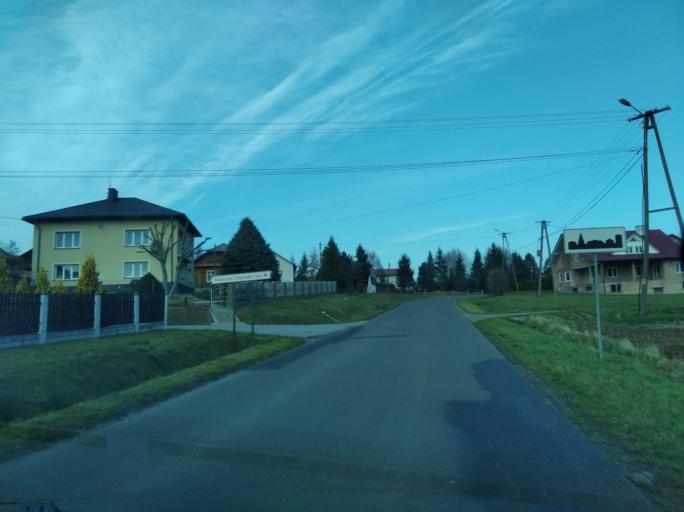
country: PL
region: Subcarpathian Voivodeship
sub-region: Powiat ropczycko-sedziszowski
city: Iwierzyce
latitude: 50.0209
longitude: 21.7530
